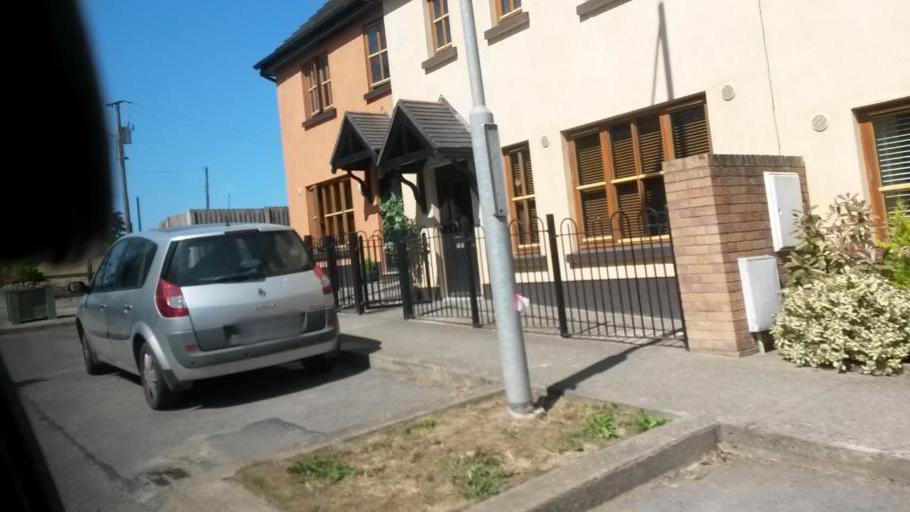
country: IE
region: Leinster
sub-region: Fingal County
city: Swords
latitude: 53.5234
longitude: -6.2683
